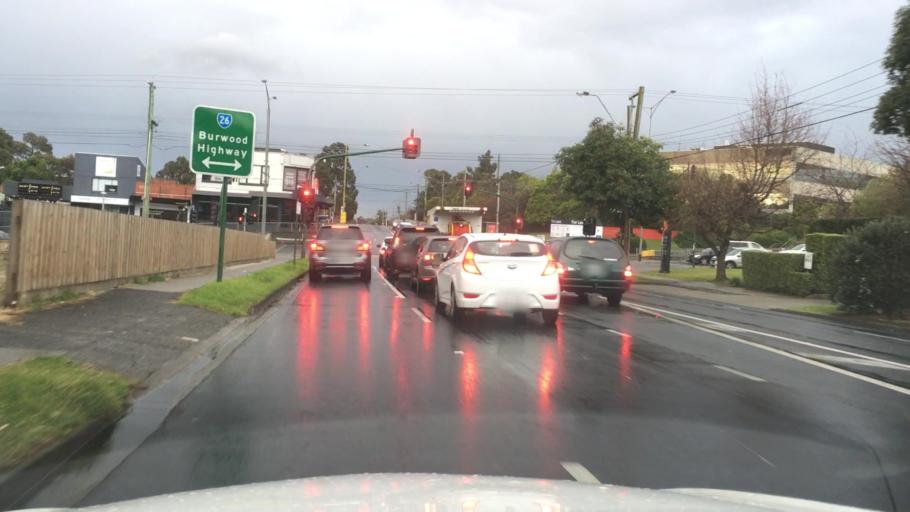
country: AU
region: Victoria
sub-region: Whitehorse
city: Burwood
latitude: -37.8512
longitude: 145.1198
